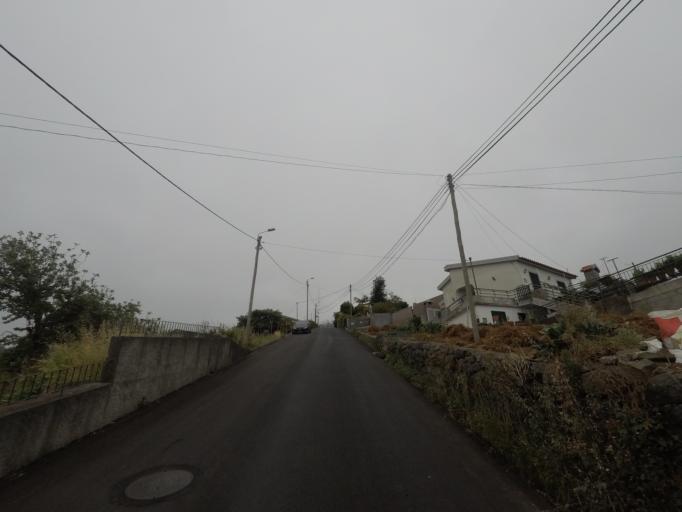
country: PT
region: Madeira
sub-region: Camara de Lobos
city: Curral das Freiras
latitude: 32.6807
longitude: -16.9467
